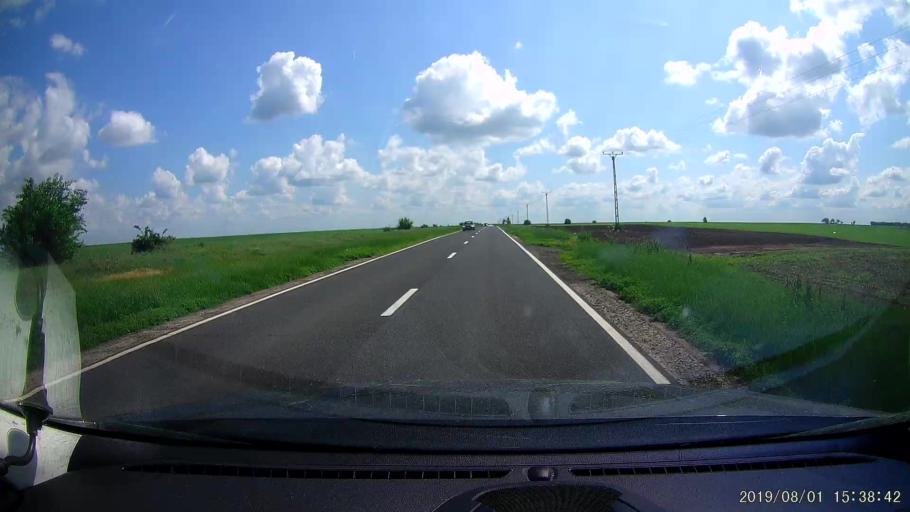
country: RO
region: Braila
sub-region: Comuna Insuratei
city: Insuratei
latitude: 44.8755
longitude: 27.5723
